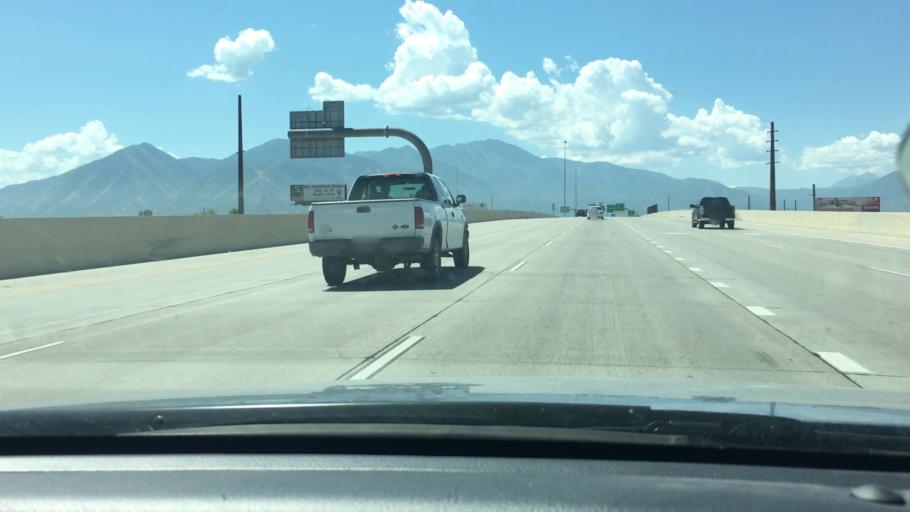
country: US
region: Utah
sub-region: Utah County
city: Spanish Fork
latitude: 40.1399
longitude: -111.6470
